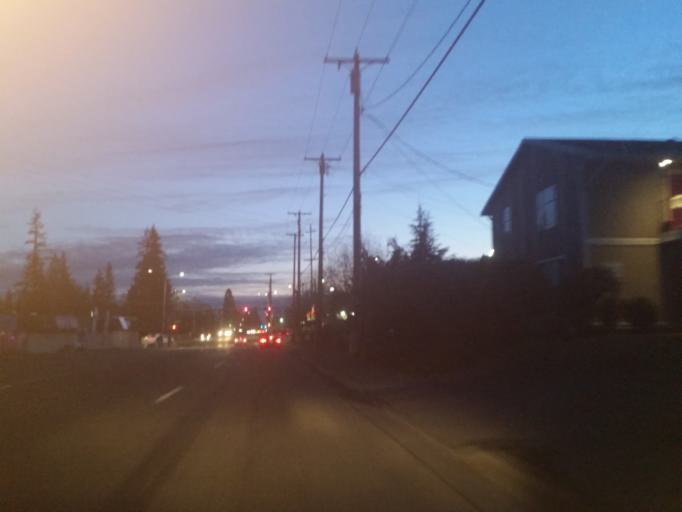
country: US
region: Washington
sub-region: Snohomish County
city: Martha Lake
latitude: 47.9116
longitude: -122.2392
